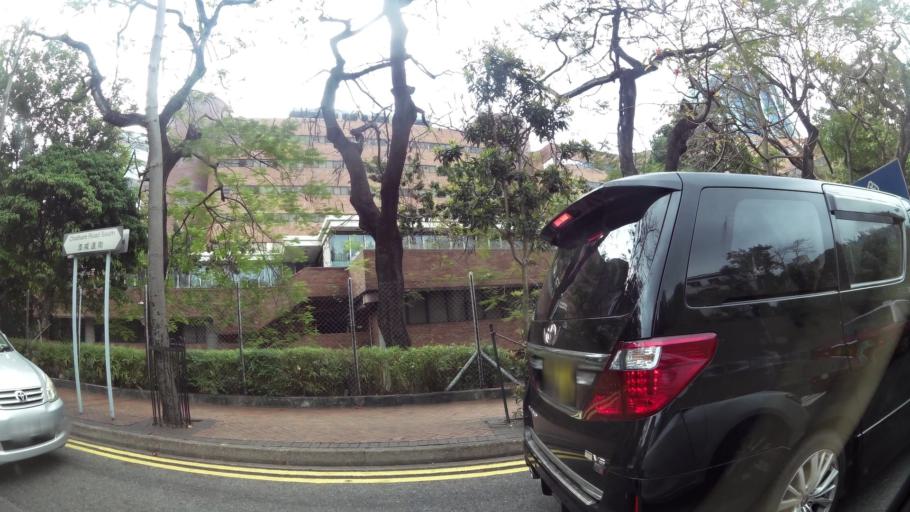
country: HK
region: Kowloon City
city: Kowloon
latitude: 22.3038
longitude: 114.1781
